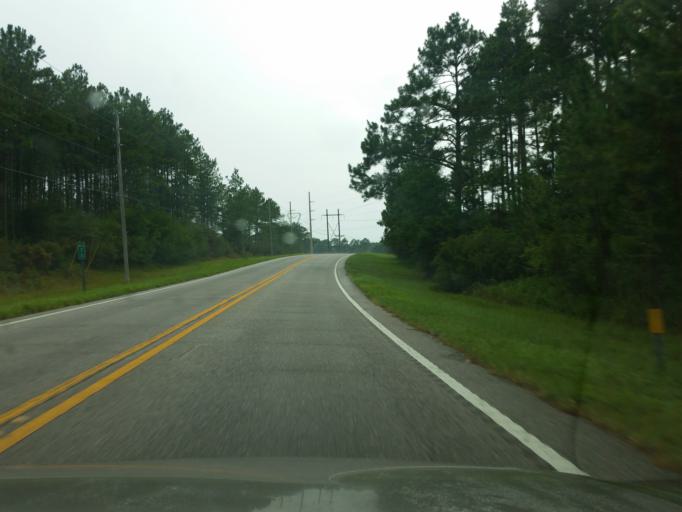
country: US
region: Alabama
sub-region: Baldwin County
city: Elberta
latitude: 30.5269
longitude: -87.5111
